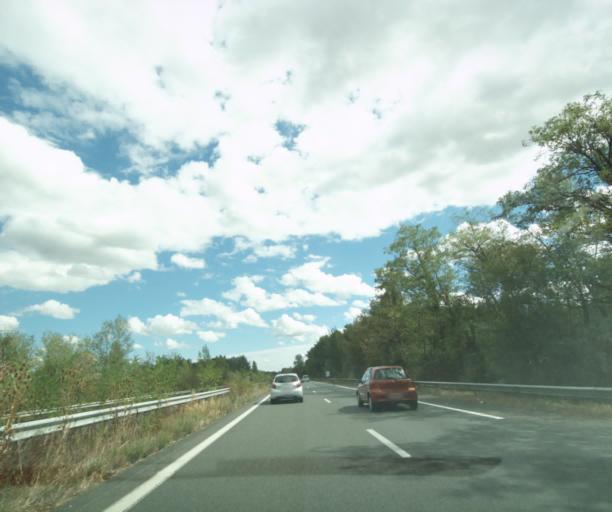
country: FR
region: Aquitaine
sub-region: Departement du Lot-et-Garonne
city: Meilhan-sur-Garonne
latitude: 44.4981
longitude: -0.0223
